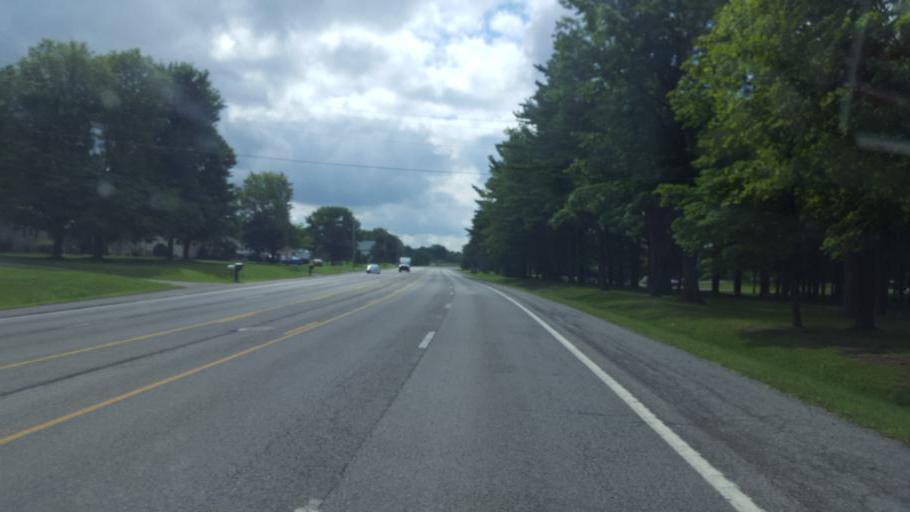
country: US
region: Ohio
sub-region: Richland County
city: Ontario
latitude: 40.8323
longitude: -82.6024
